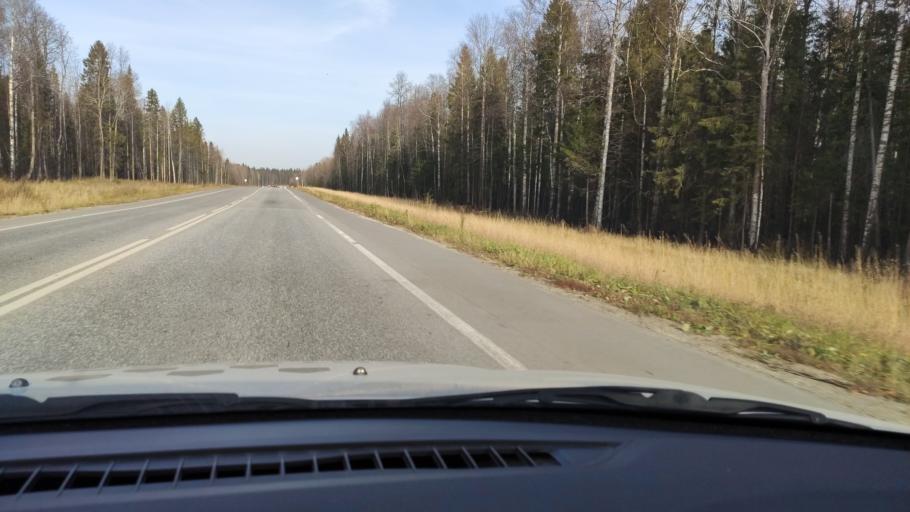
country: RU
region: Perm
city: Novyye Lyady
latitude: 58.0446
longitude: 56.5443
